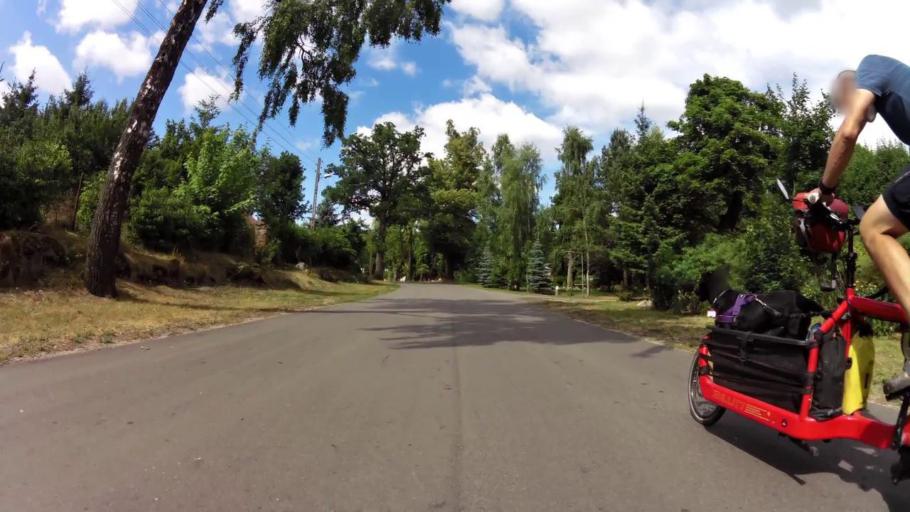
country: PL
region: West Pomeranian Voivodeship
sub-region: Powiat lobeski
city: Lobez
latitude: 53.6250
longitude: 15.6794
